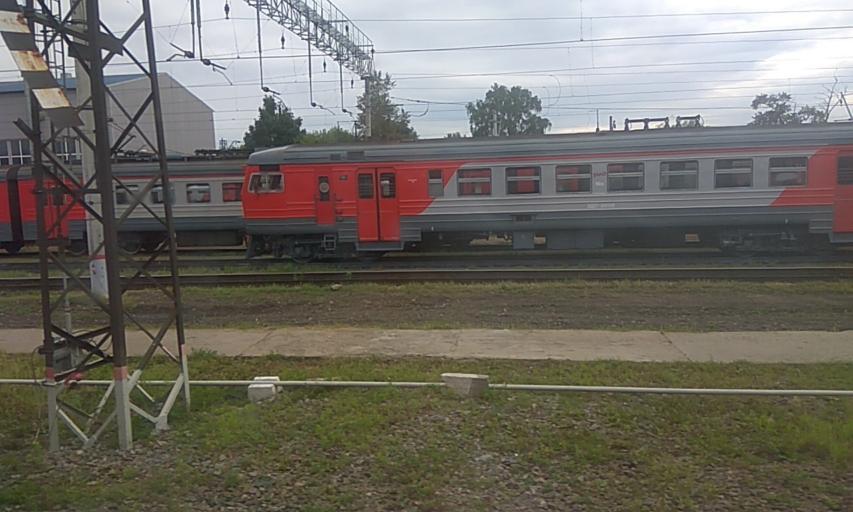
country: RU
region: Moskovskaya
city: Ramenskoye
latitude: 55.5579
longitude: 38.2467
